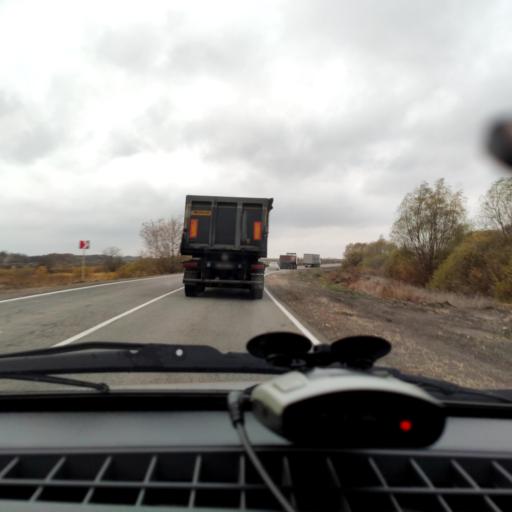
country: RU
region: Voronezj
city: Shilovo
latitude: 51.4519
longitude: 38.9798
